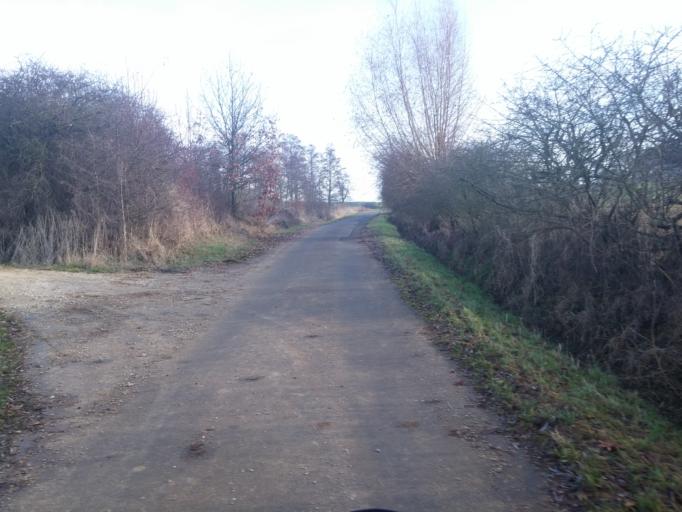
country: DE
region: Bavaria
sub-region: Upper Franconia
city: Untersiemau
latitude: 50.1761
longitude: 10.9713
